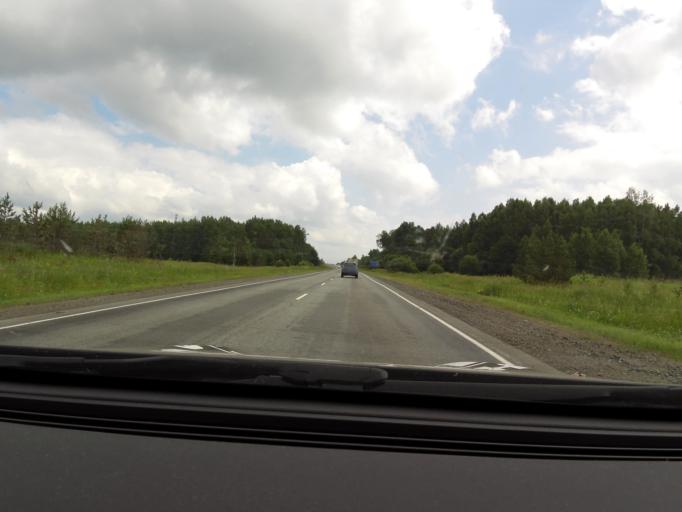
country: RU
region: Sverdlovsk
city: Achit
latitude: 56.8629
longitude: 57.6844
